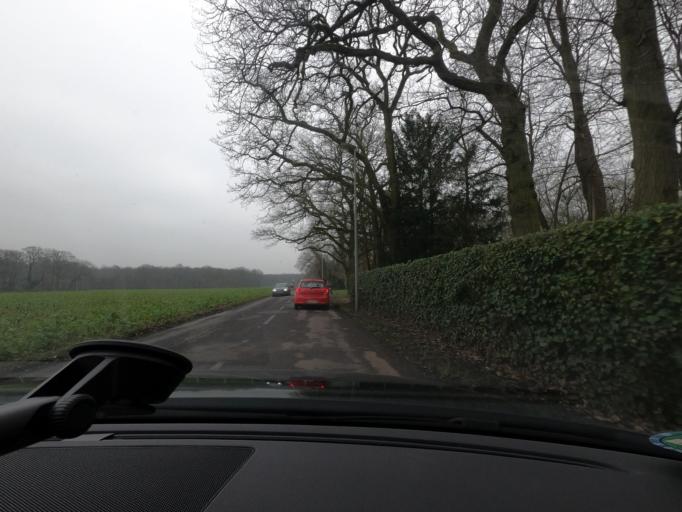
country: DE
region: North Rhine-Westphalia
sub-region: Regierungsbezirk Dusseldorf
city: Krefeld
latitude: 51.3937
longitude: 6.5382
